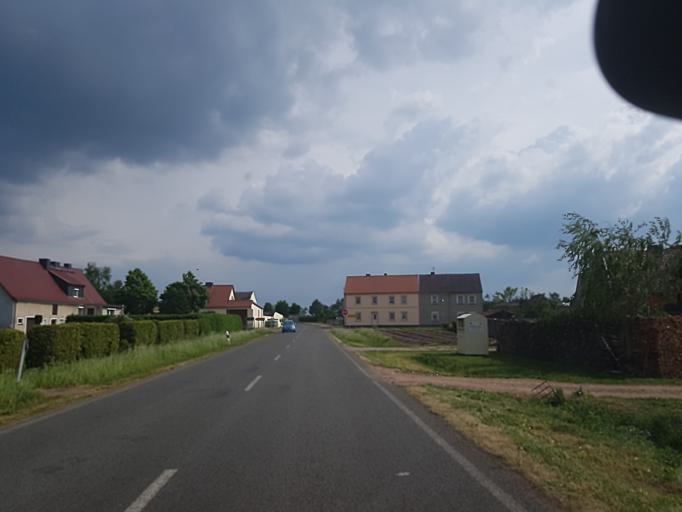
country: DE
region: Saxony-Anhalt
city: Rodleben
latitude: 51.9872
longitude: 12.2338
